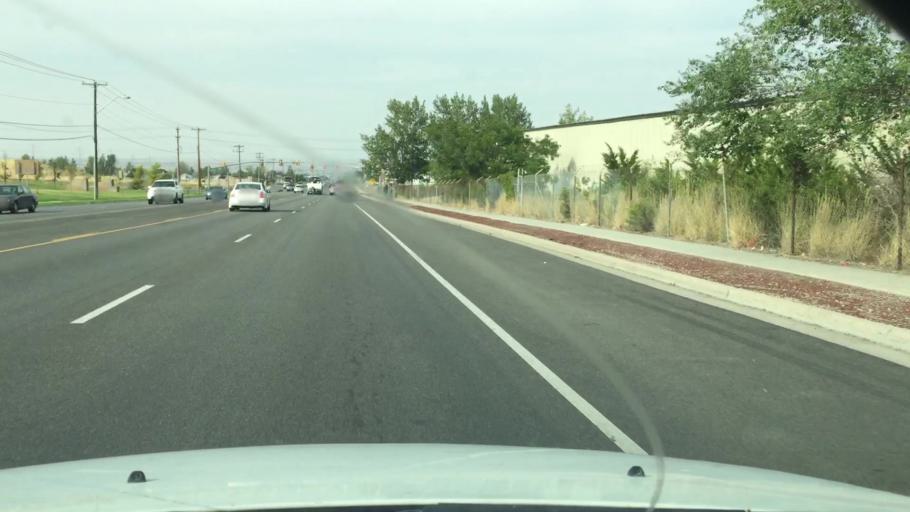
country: US
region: Utah
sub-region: Salt Lake County
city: Kearns
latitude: 40.6657
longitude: -112.0246
